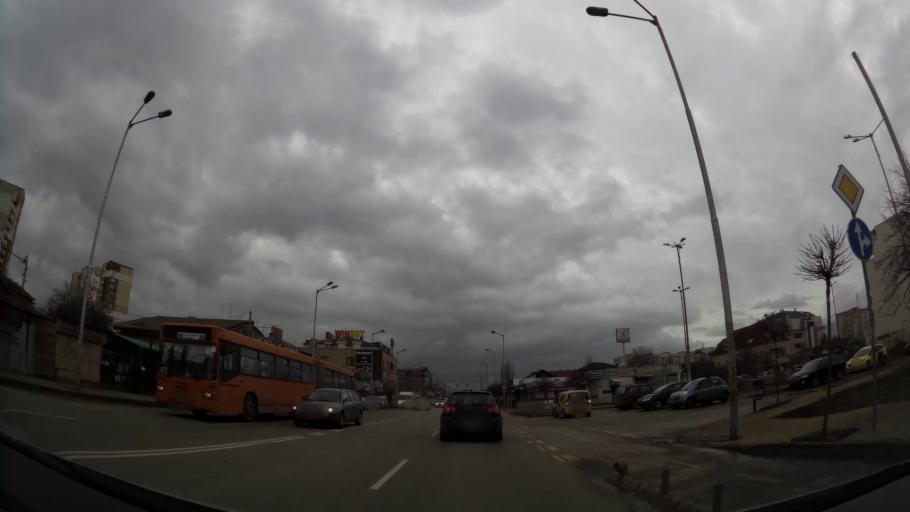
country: BG
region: Sofia-Capital
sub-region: Stolichna Obshtina
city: Sofia
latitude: 42.7335
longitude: 23.2949
